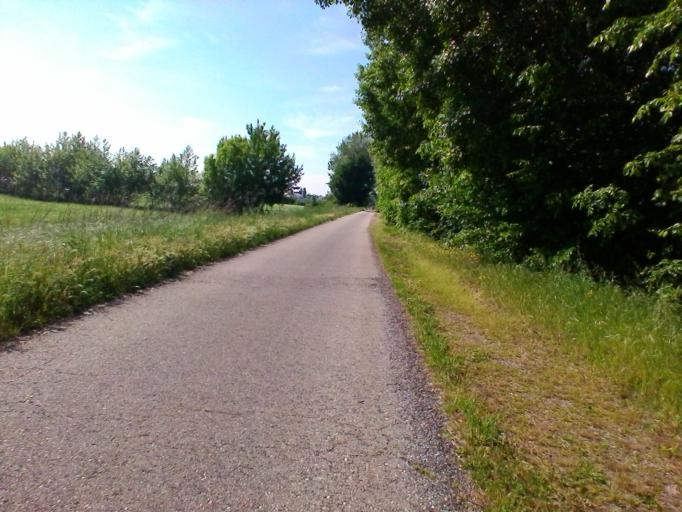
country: IT
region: Lombardy
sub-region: Provincia di Mantova
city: Marmirolo
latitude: 45.2331
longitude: 10.7279
